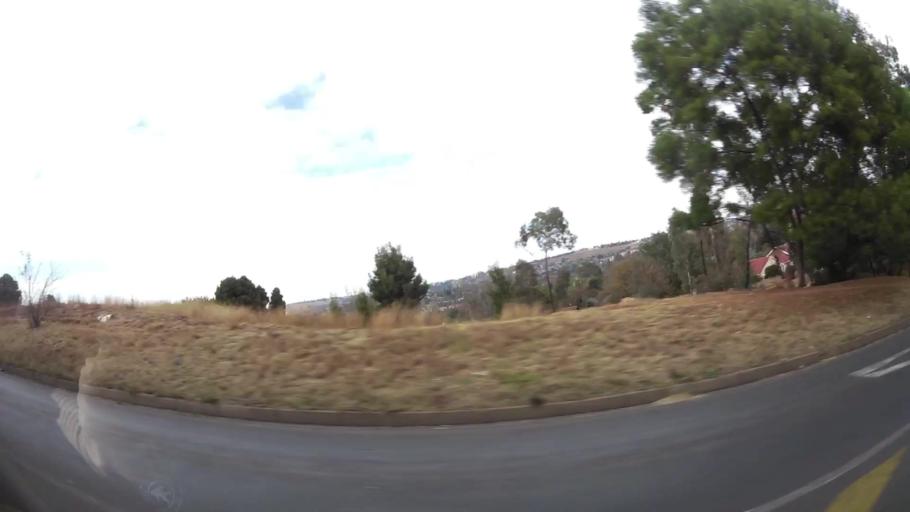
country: ZA
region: Gauteng
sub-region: City of Johannesburg Metropolitan Municipality
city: Roodepoort
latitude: -26.1075
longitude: 27.8596
